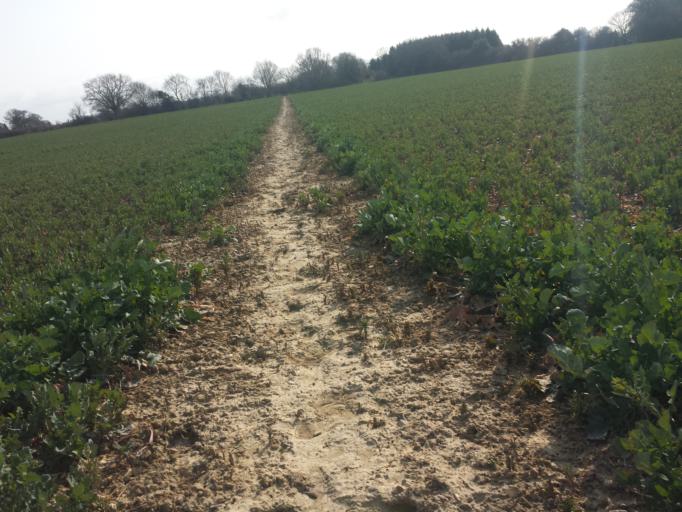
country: GB
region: England
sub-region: Essex
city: Little Clacton
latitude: 51.8904
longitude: 1.1625
